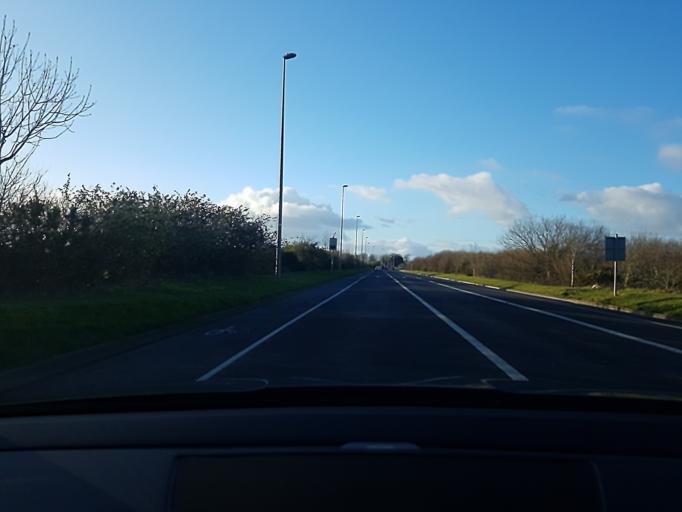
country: IE
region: Munster
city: Moyross
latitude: 52.6600
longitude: -8.6604
